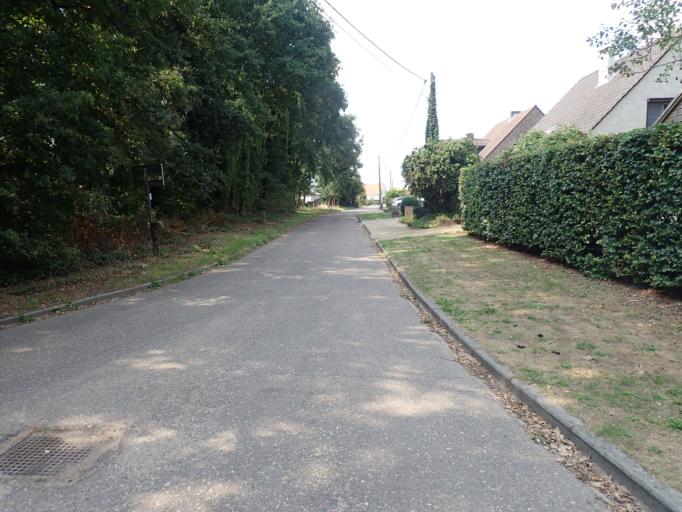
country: BE
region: Flanders
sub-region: Provincie Antwerpen
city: Meerhout
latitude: 51.1614
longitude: 5.0685
